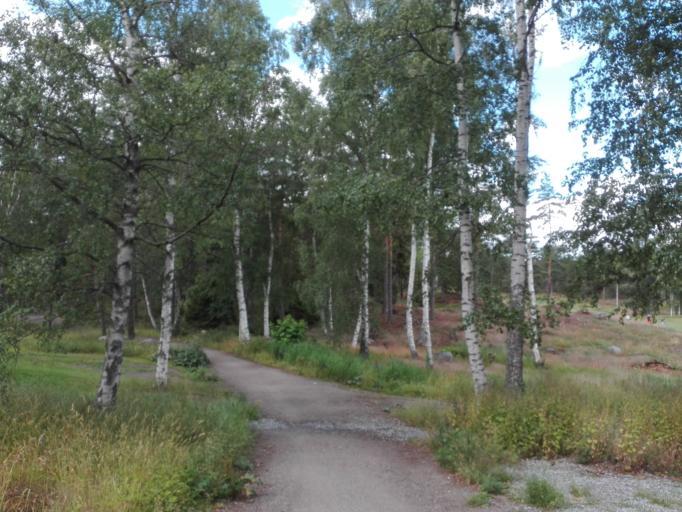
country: SE
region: Stockholm
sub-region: Nacka Kommun
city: Fisksatra
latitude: 59.2842
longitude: 18.2645
